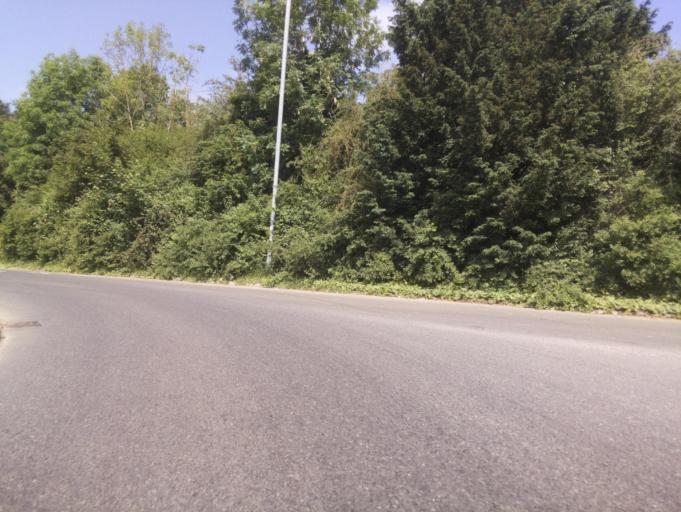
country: GB
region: England
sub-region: Somerset
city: Wincanton
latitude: 51.0536
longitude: -2.4420
